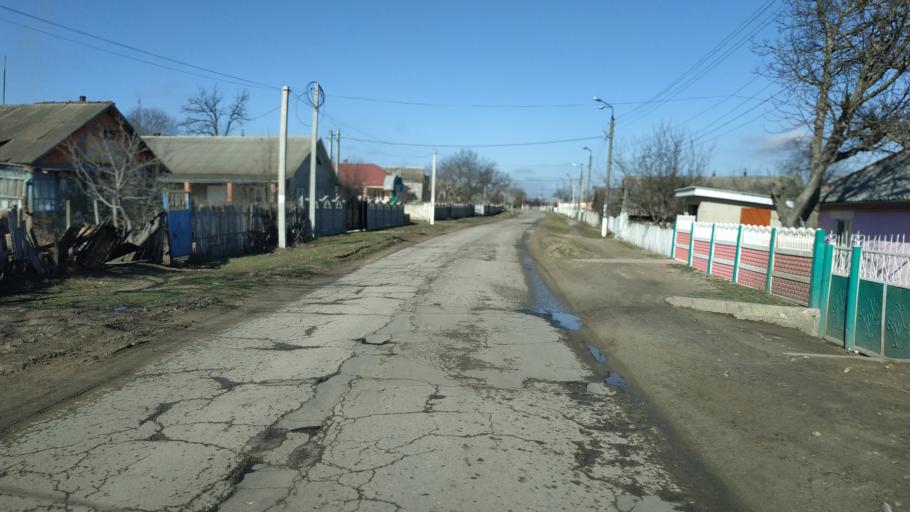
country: MD
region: Hincesti
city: Hincesti
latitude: 46.9648
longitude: 28.5994
